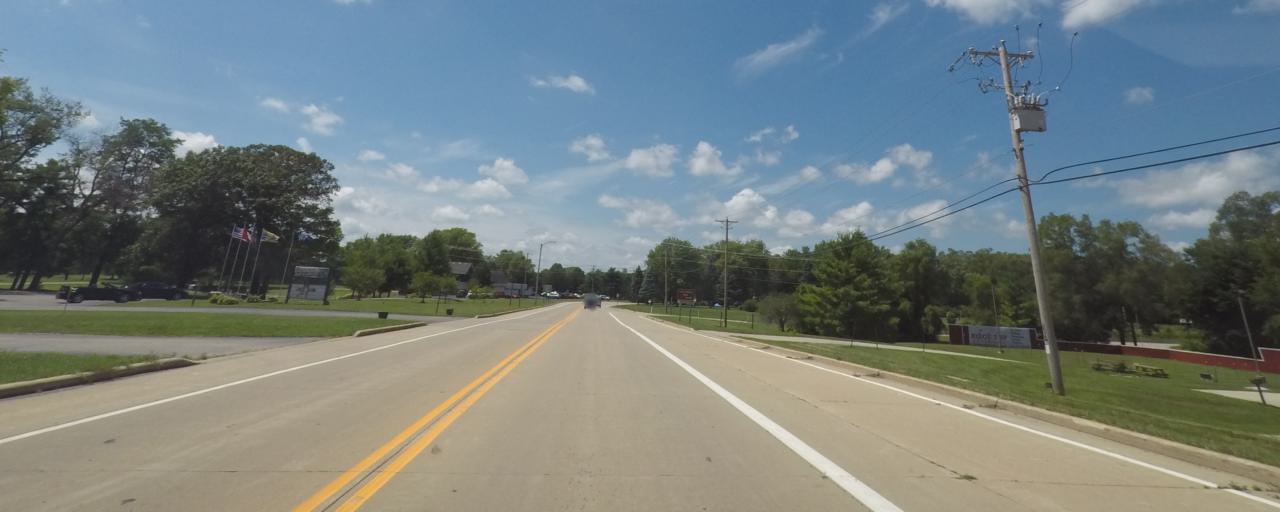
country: US
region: Wisconsin
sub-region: Jefferson County
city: Cambridge
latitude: 42.9995
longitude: -89.0043
